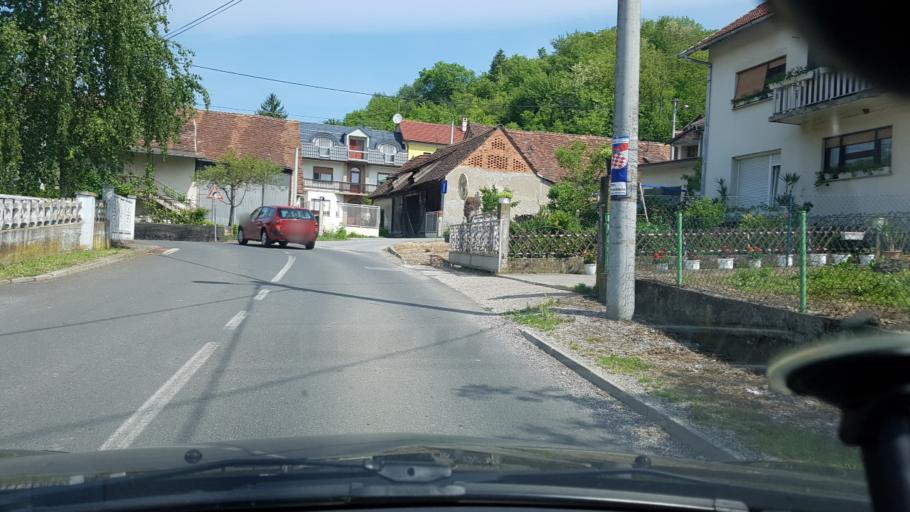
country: HR
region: Krapinsko-Zagorska
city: Marija Bistrica
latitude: 45.9395
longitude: 16.1650
